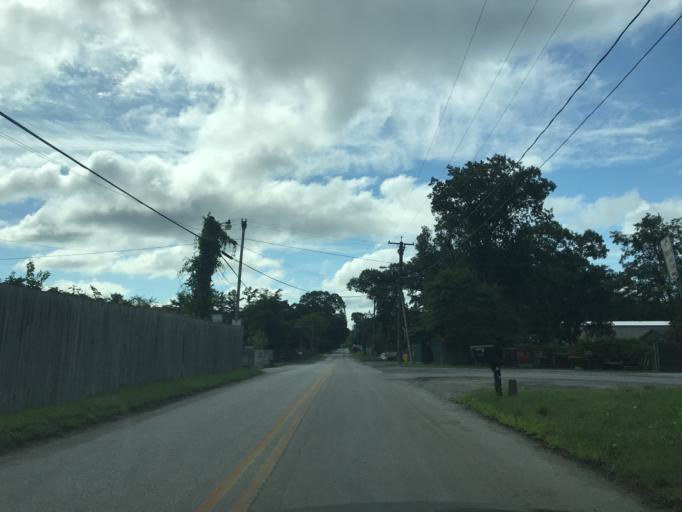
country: US
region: Maryland
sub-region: Anne Arundel County
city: Pasadena
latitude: 39.1197
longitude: -76.5661
